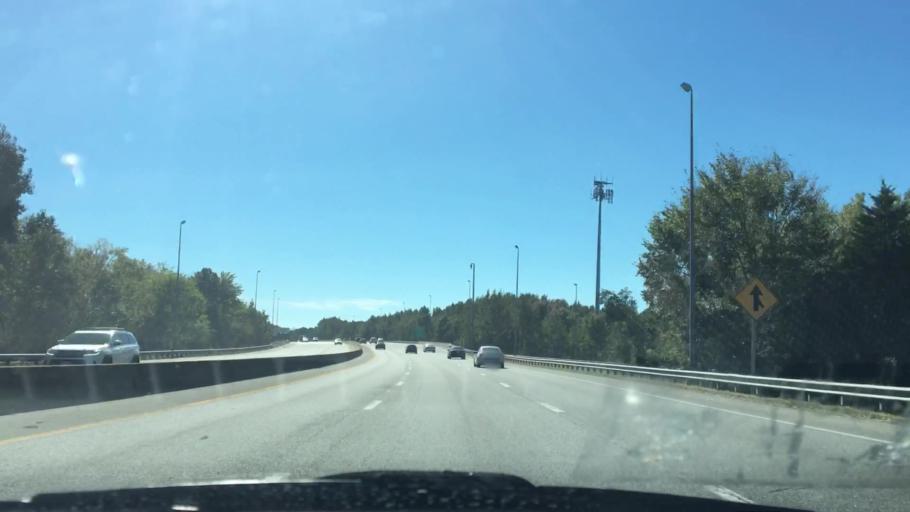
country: US
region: Virginia
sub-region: City of Portsmouth
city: Portsmouth Heights
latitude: 36.8169
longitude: -76.3464
